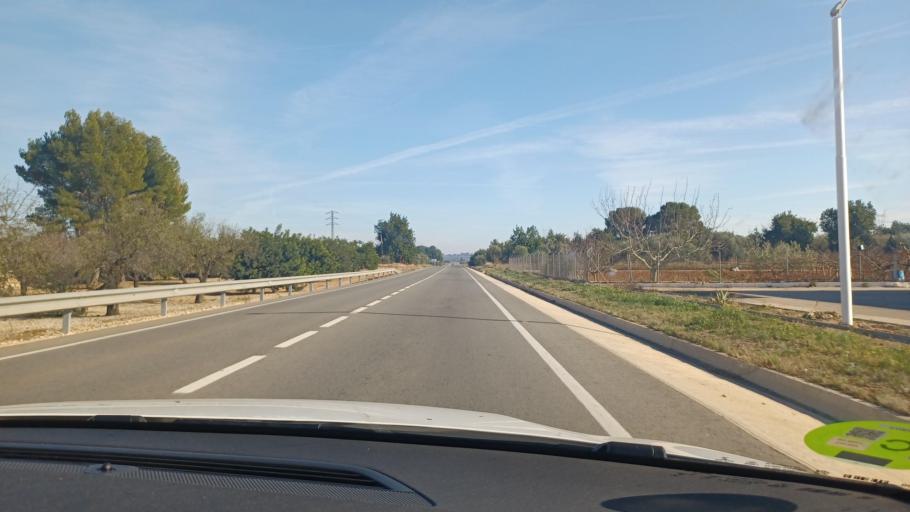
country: ES
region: Catalonia
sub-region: Provincia de Tarragona
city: Santa Barbara
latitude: 40.7169
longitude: 0.5085
